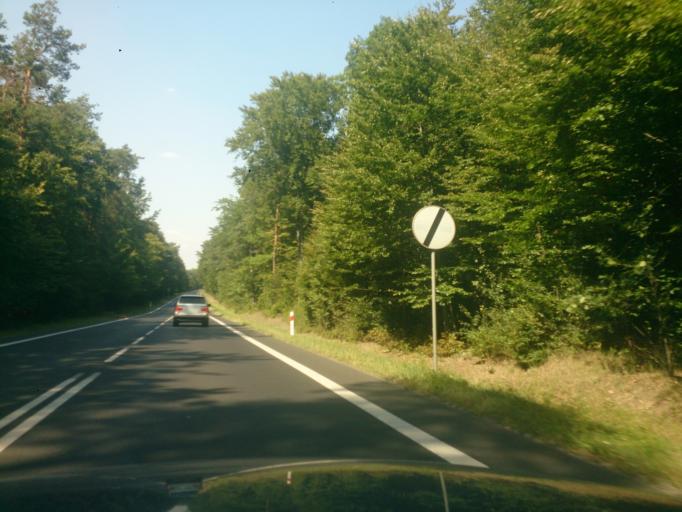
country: PL
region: Subcarpathian Voivodeship
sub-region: Powiat rzeszowski
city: Glogow Malopolski
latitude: 50.1788
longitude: 21.9223
